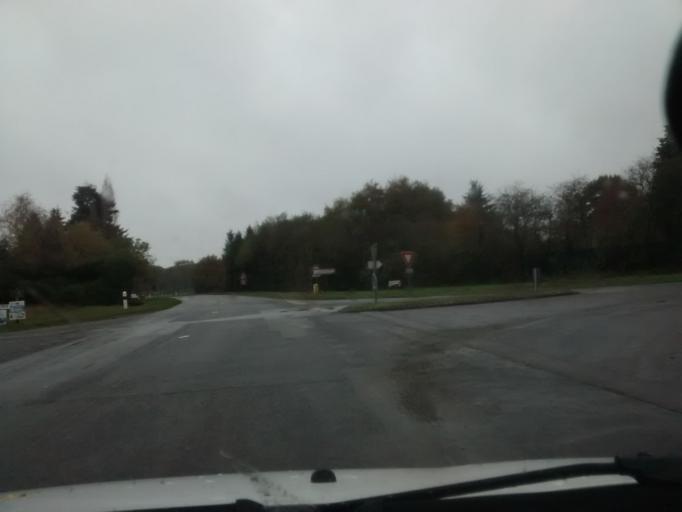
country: FR
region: Brittany
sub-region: Departement d'Ille-et-Vilaine
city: Chantepie
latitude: 48.0777
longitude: -1.6057
